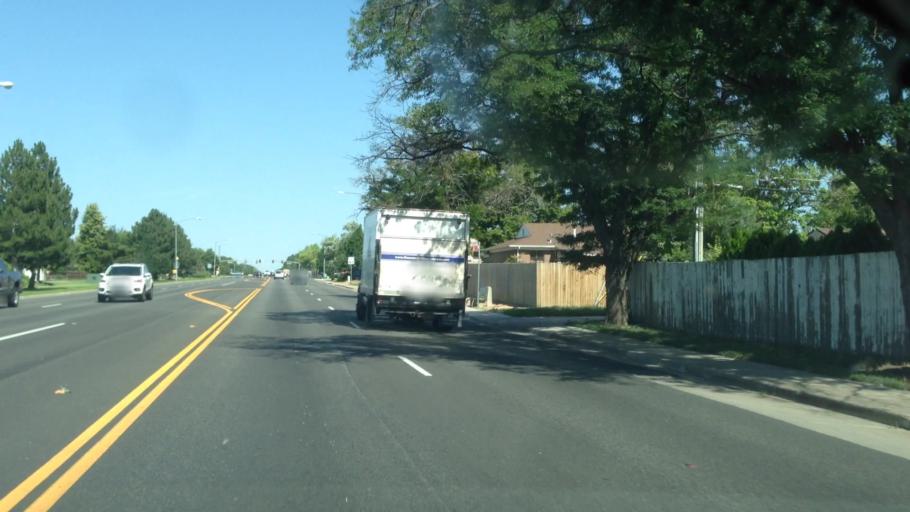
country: US
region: Colorado
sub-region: Adams County
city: Aurora
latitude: 39.7255
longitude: -104.8705
